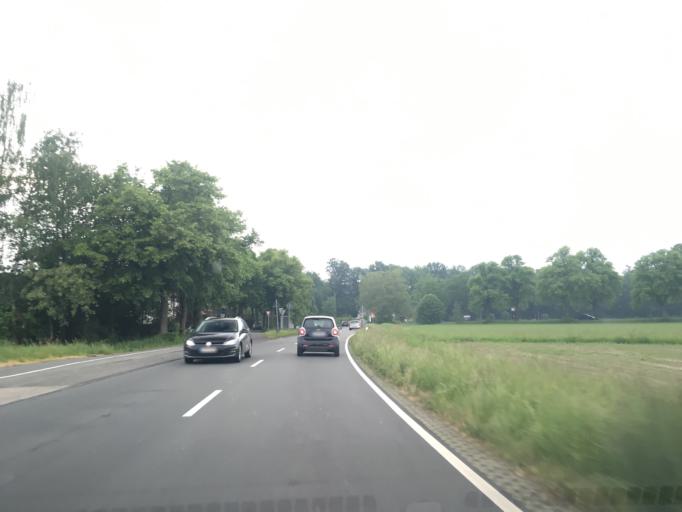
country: DE
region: North Rhine-Westphalia
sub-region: Regierungsbezirk Munster
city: Muenster
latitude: 51.9957
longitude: 7.6829
